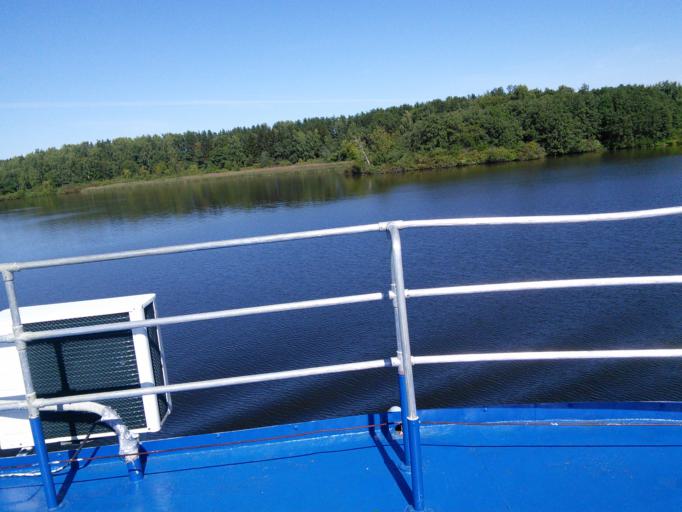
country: RU
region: Moskovskaya
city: Yermolino
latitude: 56.1323
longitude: 37.5452
